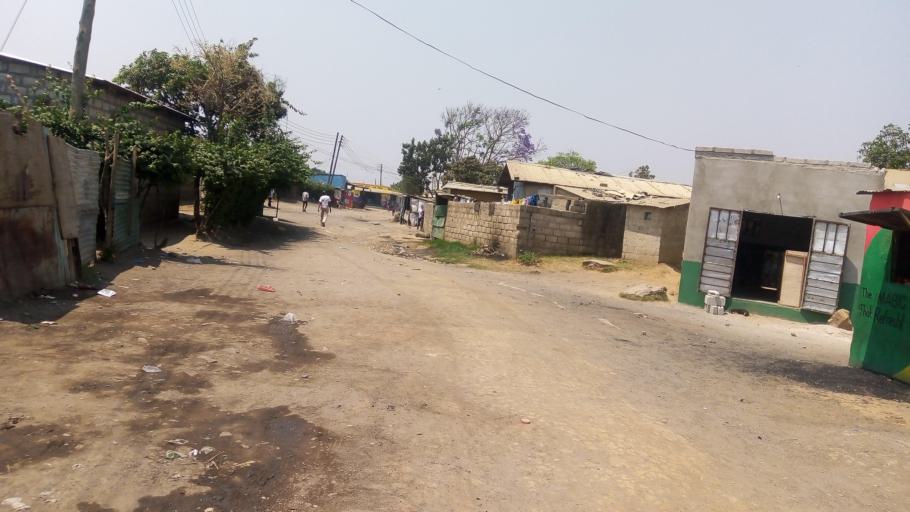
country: ZM
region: Lusaka
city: Lusaka
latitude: -15.4420
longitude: 28.3785
